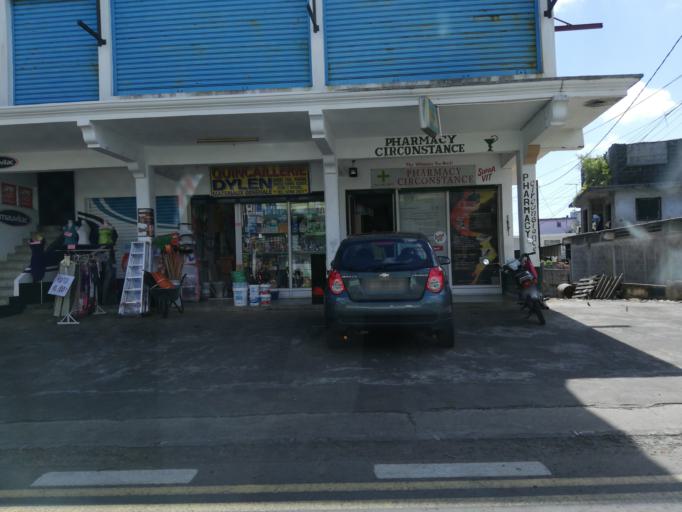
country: MU
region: Moka
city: Verdun
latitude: -20.2231
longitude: 57.5405
